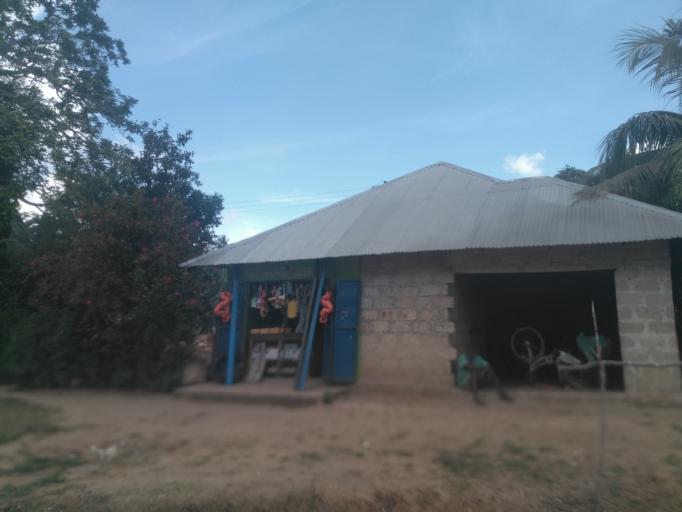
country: TZ
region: Zanzibar North
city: Gamba
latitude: -5.9750
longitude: 39.2979
